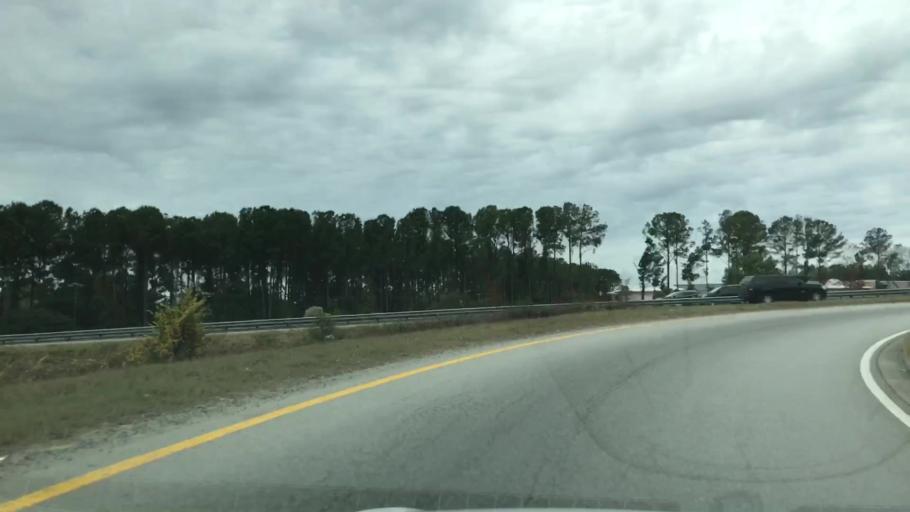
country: US
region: South Carolina
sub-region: Charleston County
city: Mount Pleasant
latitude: 32.8393
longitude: -79.8605
